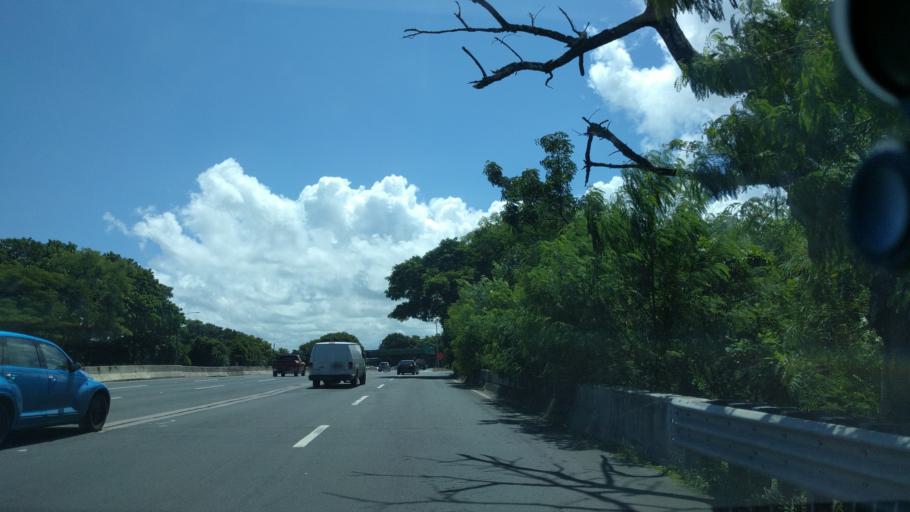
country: PR
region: San Juan
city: San Juan
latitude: 18.4417
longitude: -66.0746
